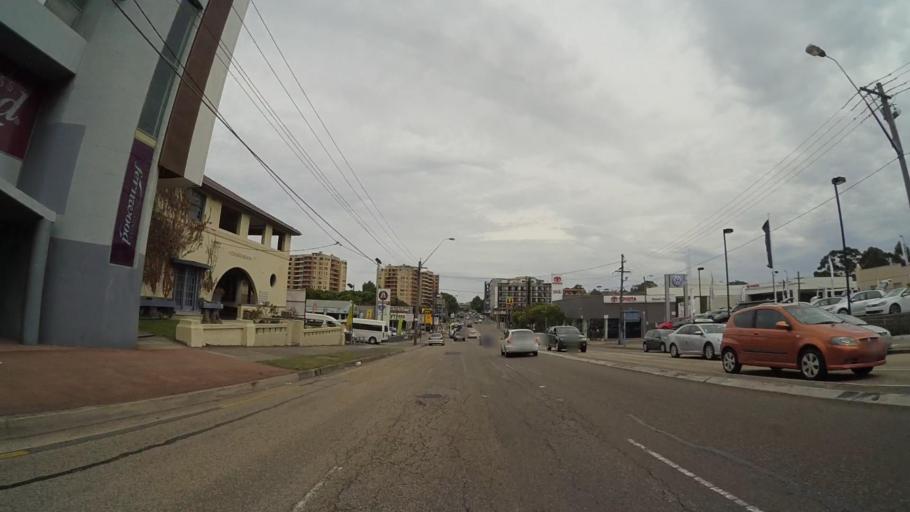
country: AU
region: New South Wales
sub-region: Rockdale
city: Banksia
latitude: -33.9554
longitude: 151.1377
